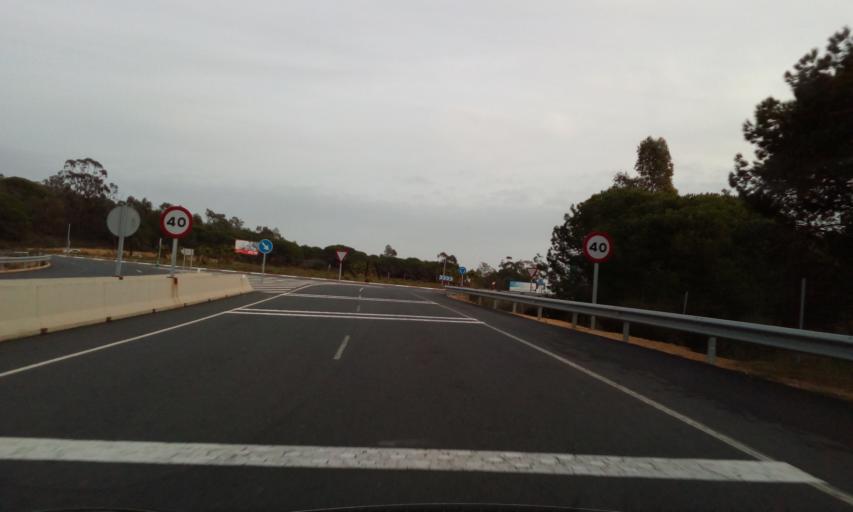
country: ES
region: Andalusia
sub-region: Provincia de Huelva
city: Lepe
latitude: 37.2140
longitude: -7.2190
